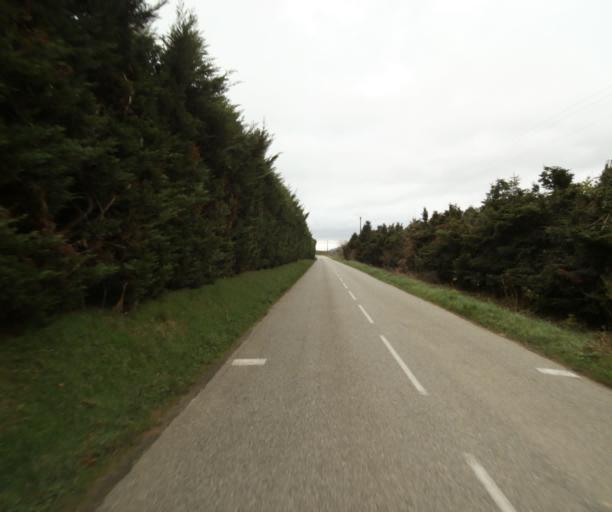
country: FR
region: Midi-Pyrenees
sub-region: Departement de l'Ariege
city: Pamiers
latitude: 43.1643
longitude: 1.6360
